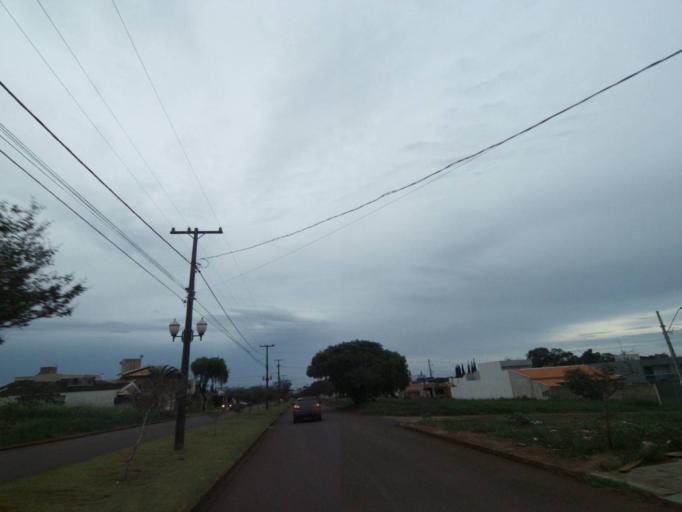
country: BR
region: Parana
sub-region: Campo Mourao
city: Campo Mourao
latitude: -24.0358
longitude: -52.3622
